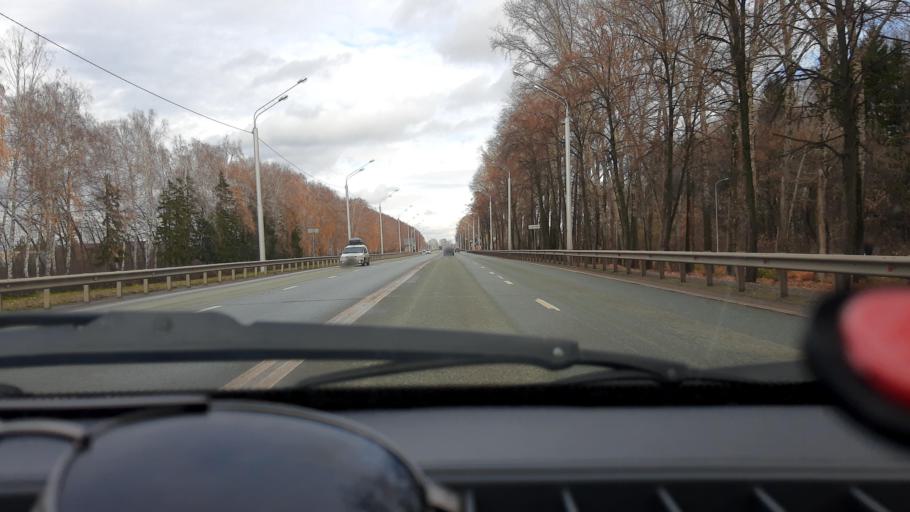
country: RU
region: Bashkortostan
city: Ufa
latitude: 54.5681
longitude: 55.8946
